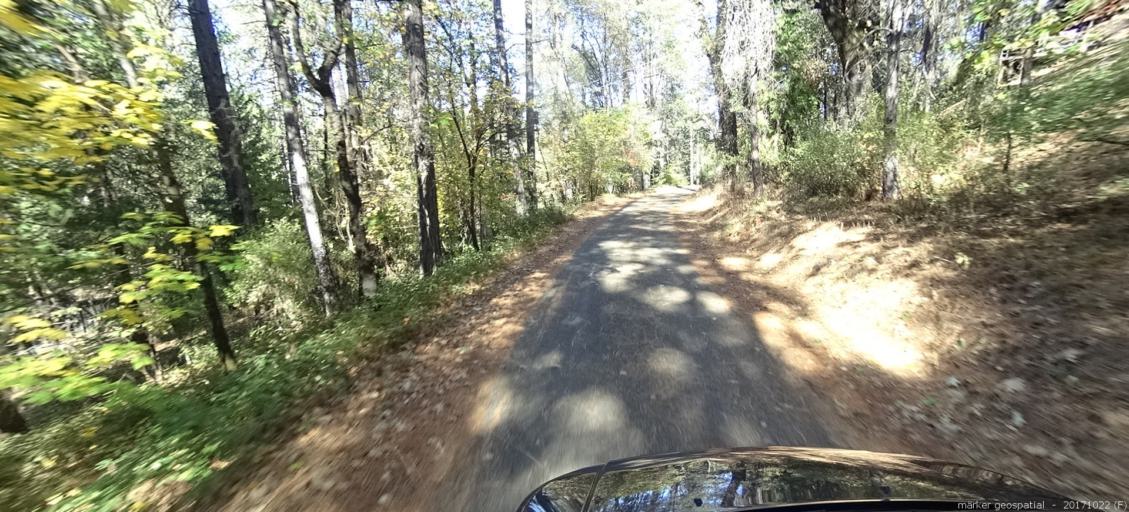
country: US
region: California
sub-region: Shasta County
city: Shasta Lake
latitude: 40.8399
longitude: -122.3605
